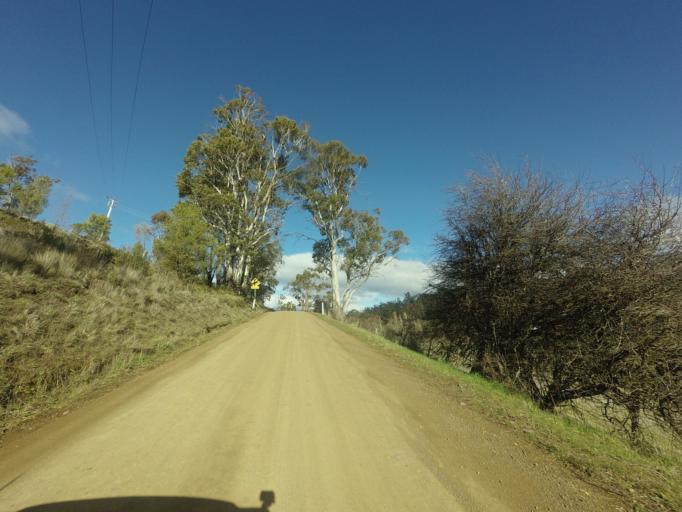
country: AU
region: Tasmania
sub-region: Derwent Valley
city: New Norfolk
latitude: -42.7063
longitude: 147.0189
